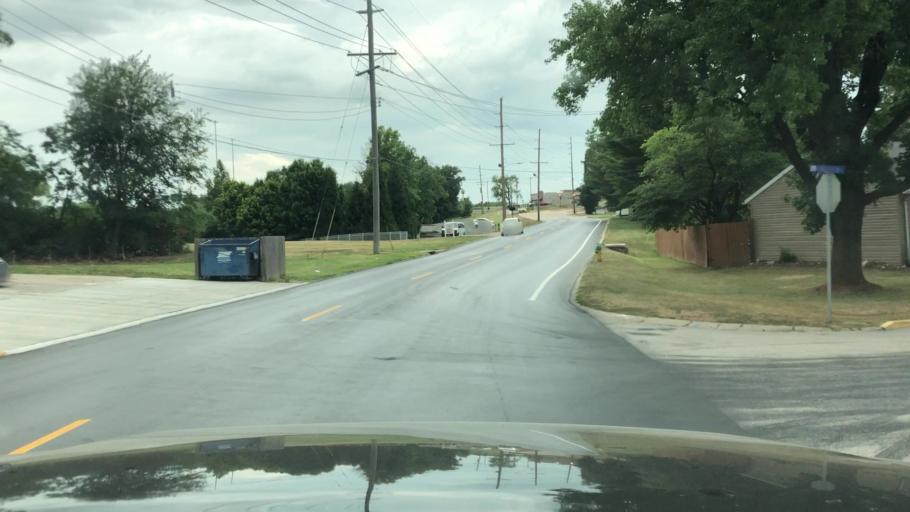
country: US
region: Missouri
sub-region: Saint Charles County
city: Saint Charles
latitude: 38.7751
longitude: -90.5075
